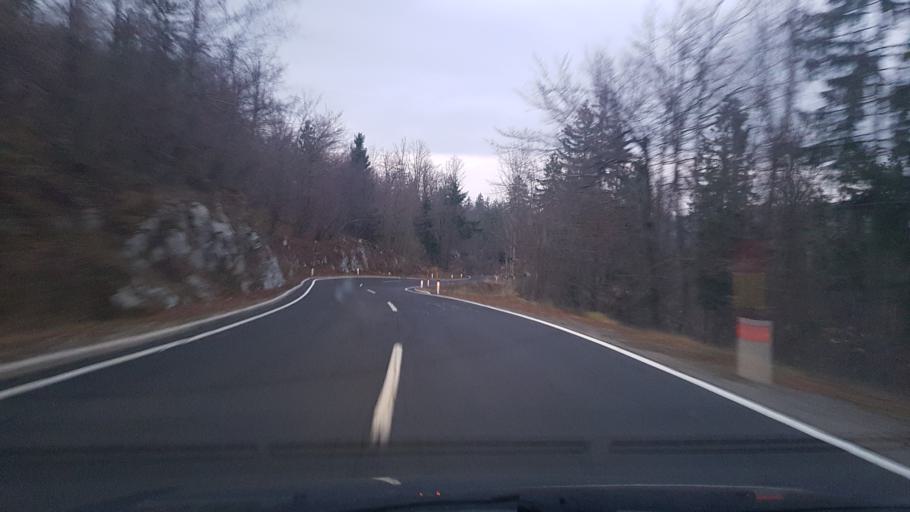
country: SI
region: Idrija
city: Idrija
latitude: 45.9482
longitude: 14.0775
